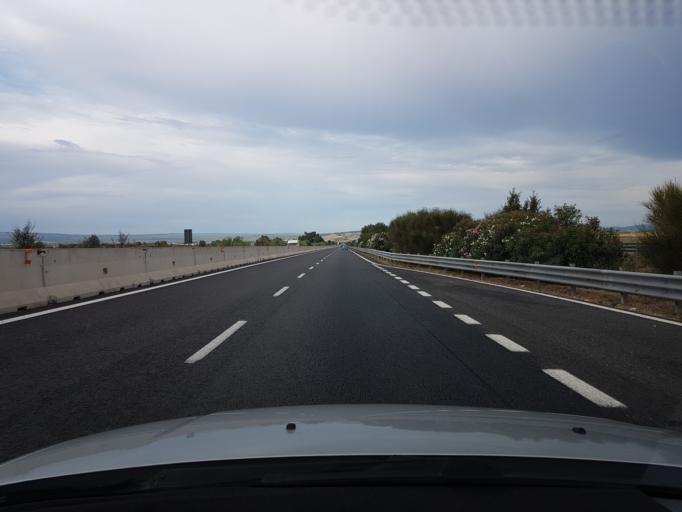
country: IT
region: Sardinia
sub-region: Provincia di Oristano
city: Tramatza
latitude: 39.9836
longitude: 8.6336
